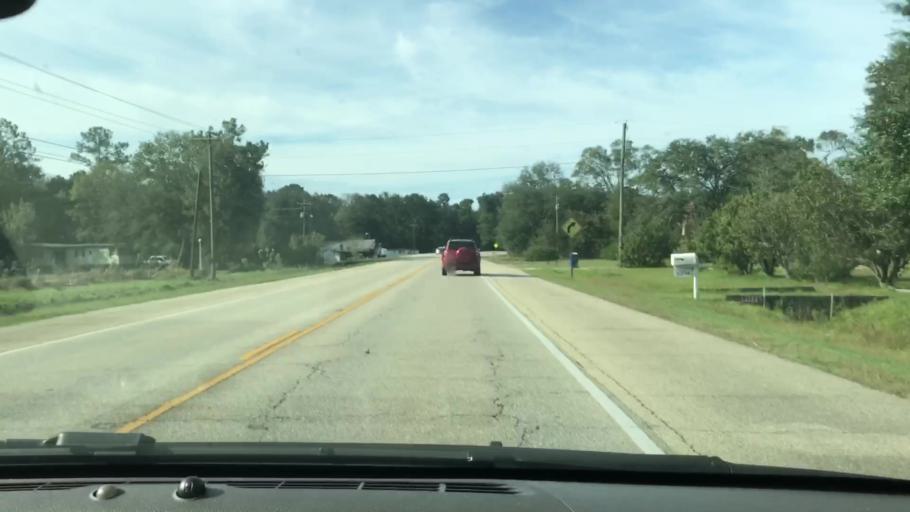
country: US
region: Louisiana
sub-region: Saint Tammany Parish
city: Pearl River
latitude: 30.4646
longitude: -89.8108
